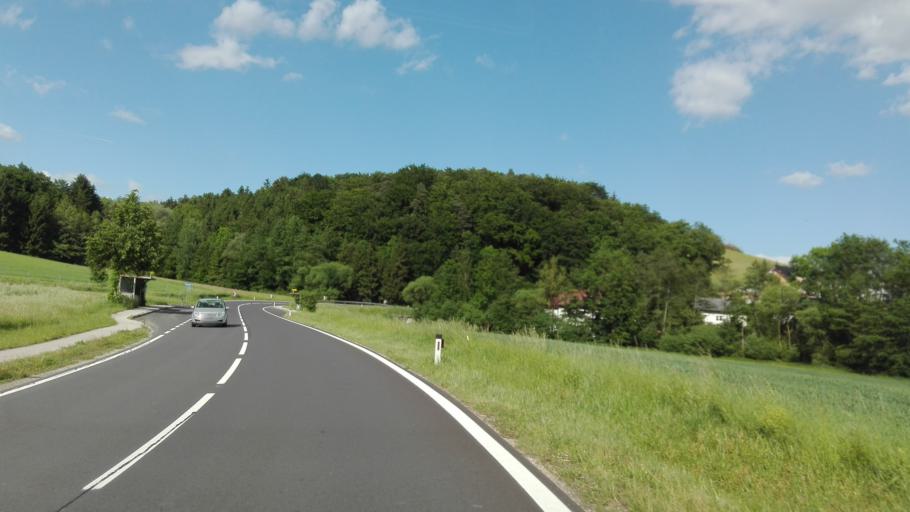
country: AT
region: Upper Austria
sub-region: Politischer Bezirk Urfahr-Umgebung
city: Gallneukirchen
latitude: 48.3373
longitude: 14.3766
